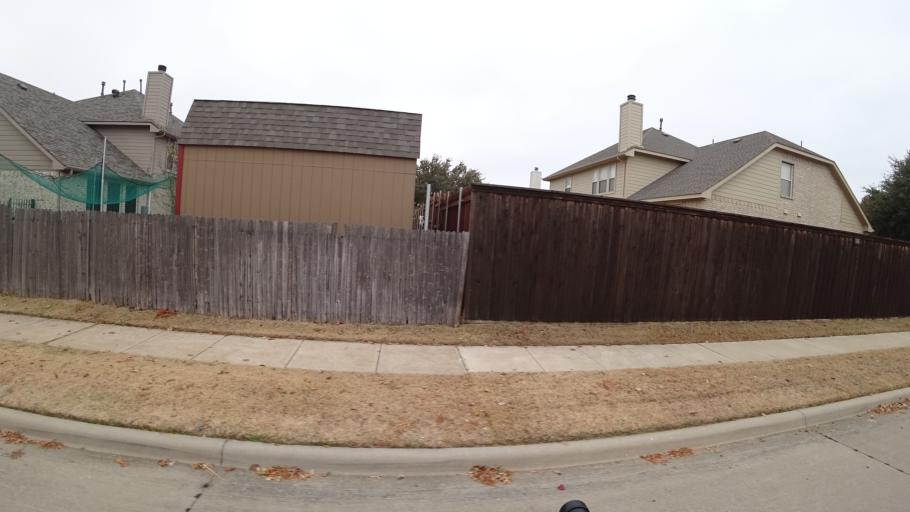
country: US
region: Texas
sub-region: Denton County
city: The Colony
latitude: 33.0696
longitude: -96.9000
